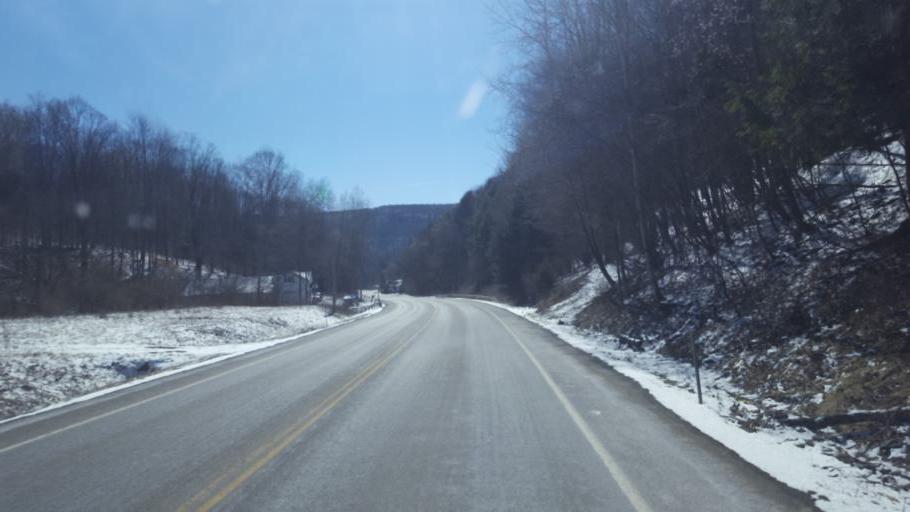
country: US
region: New York
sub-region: Allegany County
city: Andover
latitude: 42.0459
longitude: -77.7884
